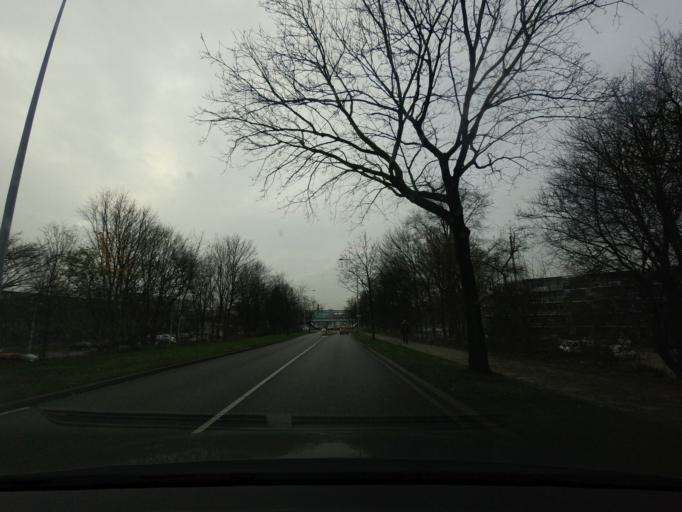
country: NL
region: North Holland
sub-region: Gemeente Amsterdam
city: Amsterdam-Zuidoost
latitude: 52.2990
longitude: 4.9624
